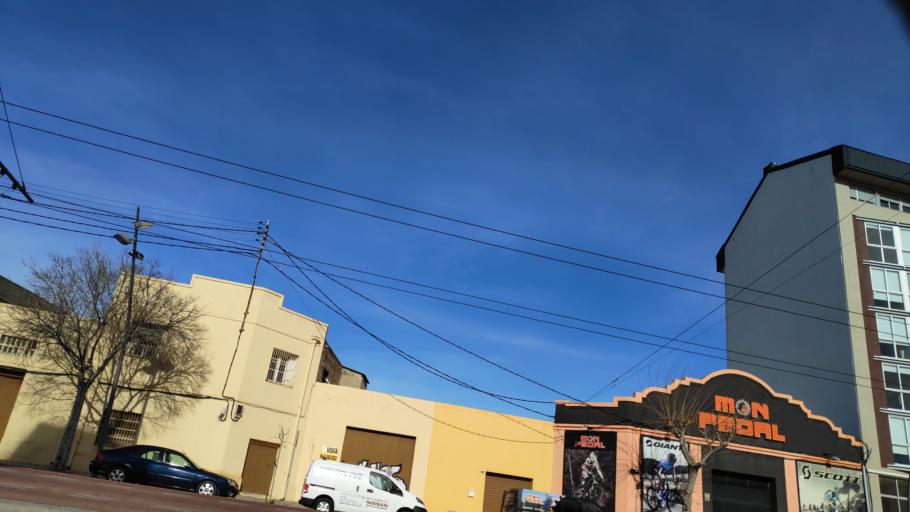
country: ES
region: Valencia
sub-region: Provincia de Castello
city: Castello de la Plana
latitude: 39.9901
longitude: -0.0529
